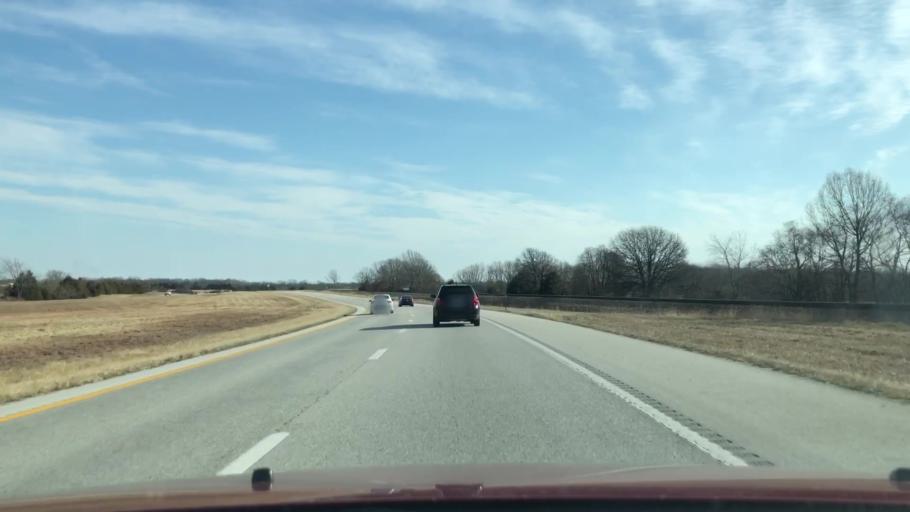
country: US
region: Missouri
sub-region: Webster County
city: Seymour
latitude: 37.1293
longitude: -92.7339
